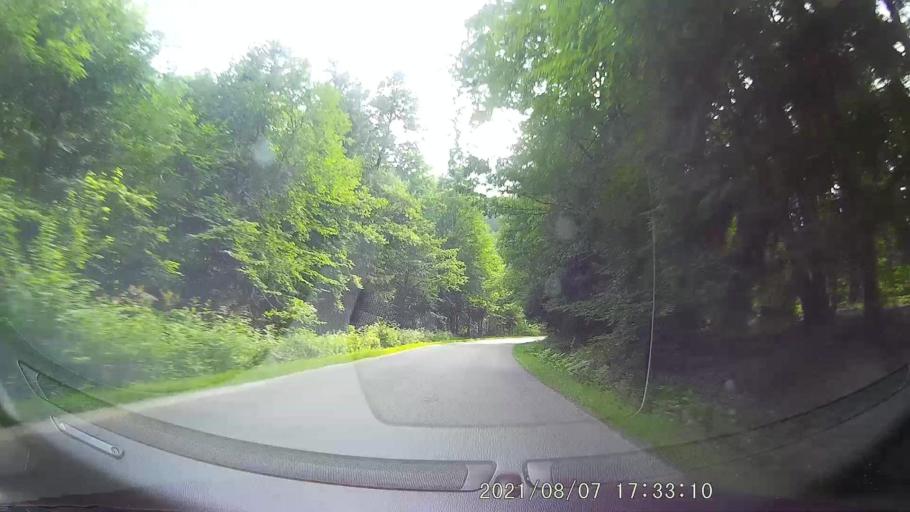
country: PL
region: Lower Silesian Voivodeship
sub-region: Powiat klodzki
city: Polanica-Zdroj
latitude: 50.3986
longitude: 16.4930
